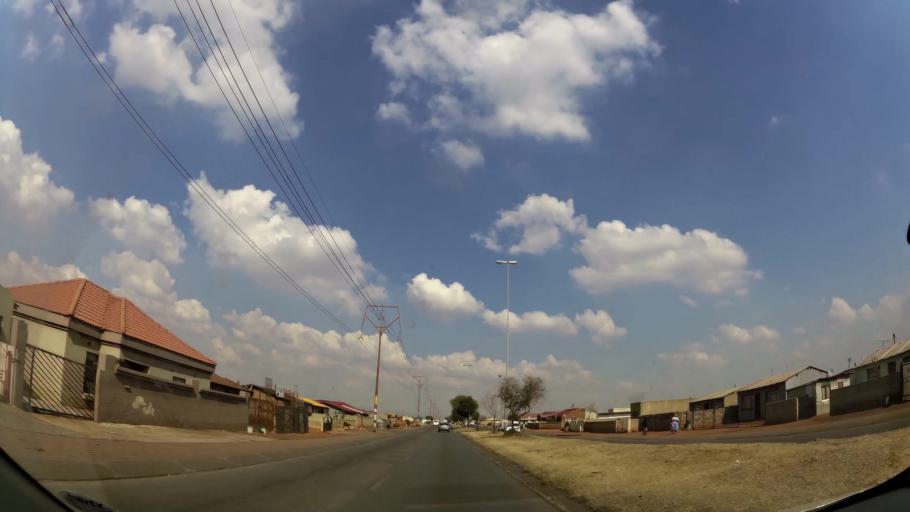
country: ZA
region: Gauteng
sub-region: Ekurhuleni Metropolitan Municipality
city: Germiston
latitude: -26.3502
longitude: 28.1619
